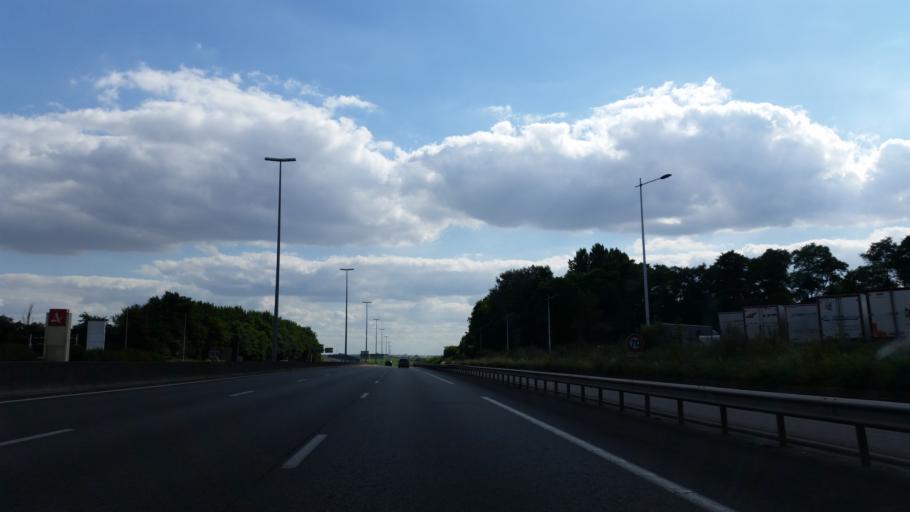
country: FR
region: Nord-Pas-de-Calais
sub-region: Departement du Pas-de-Calais
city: Feuchy
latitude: 50.2623
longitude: 2.8638
